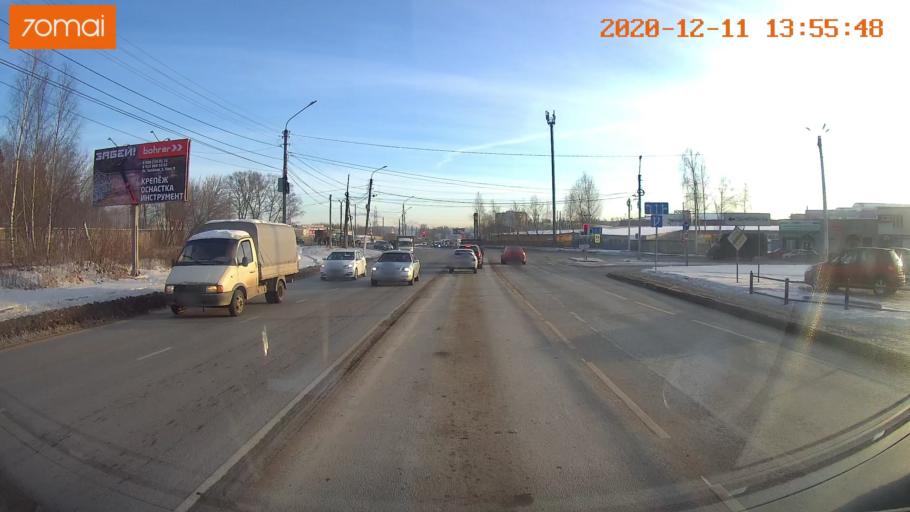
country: RU
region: Kostroma
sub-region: Kostromskoy Rayon
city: Kostroma
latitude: 57.7801
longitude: 40.9683
